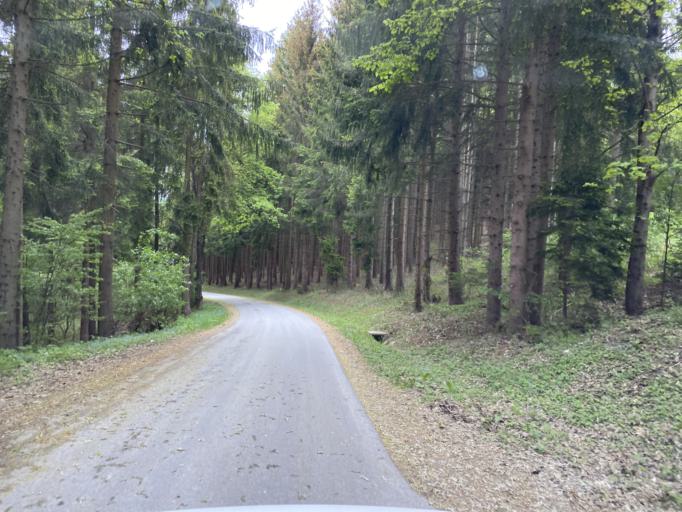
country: AT
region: Styria
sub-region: Politischer Bezirk Weiz
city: Baierdorf-Umgebung
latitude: 47.3095
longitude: 15.7108
